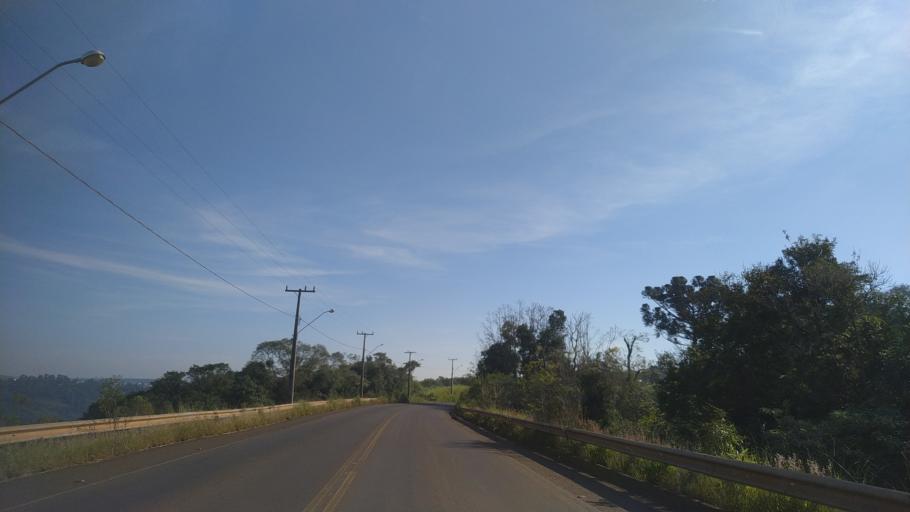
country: BR
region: Santa Catarina
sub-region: Chapeco
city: Chapeco
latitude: -27.1245
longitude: -52.6331
